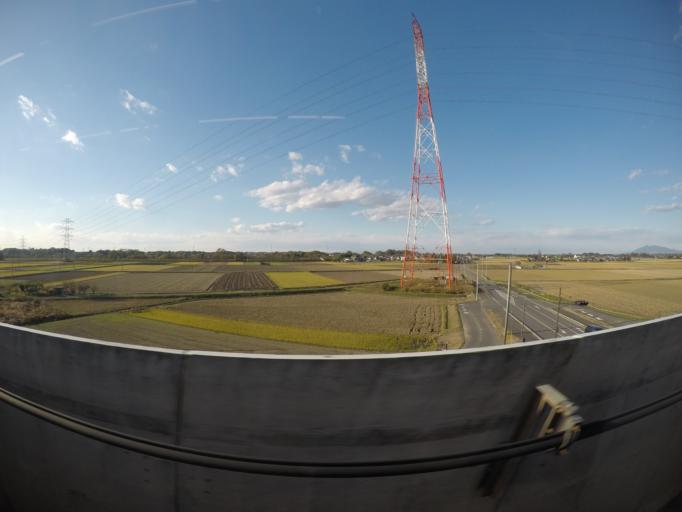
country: JP
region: Ibaraki
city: Moriya
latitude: 35.9674
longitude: 140.0091
